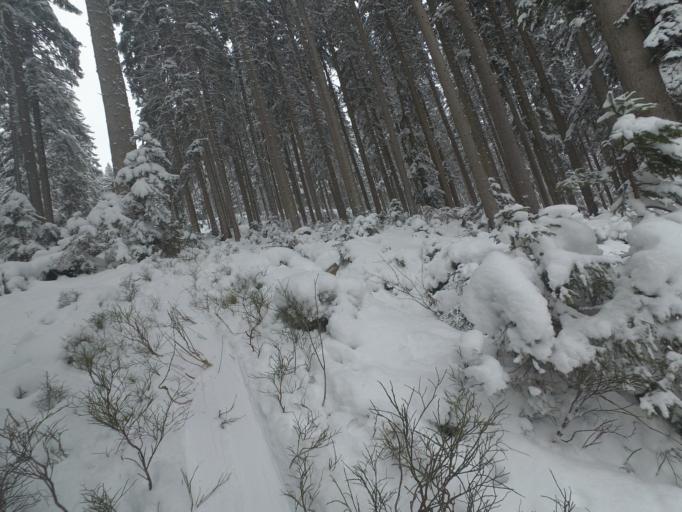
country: AT
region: Salzburg
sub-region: Politischer Bezirk Sankt Johann im Pongau
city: Wagrain
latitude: 47.3207
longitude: 13.2784
